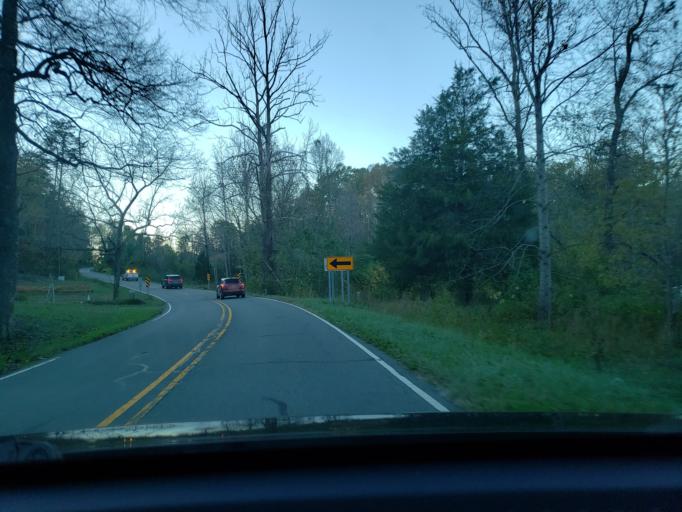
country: US
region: North Carolina
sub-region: Stokes County
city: Danbury
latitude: 36.4233
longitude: -80.2362
